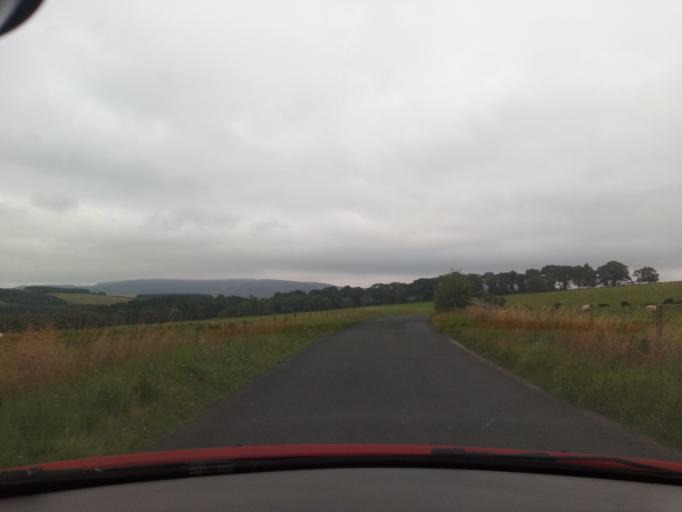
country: GB
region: England
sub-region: Northumberland
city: Otterburn
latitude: 55.3123
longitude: -2.0631
